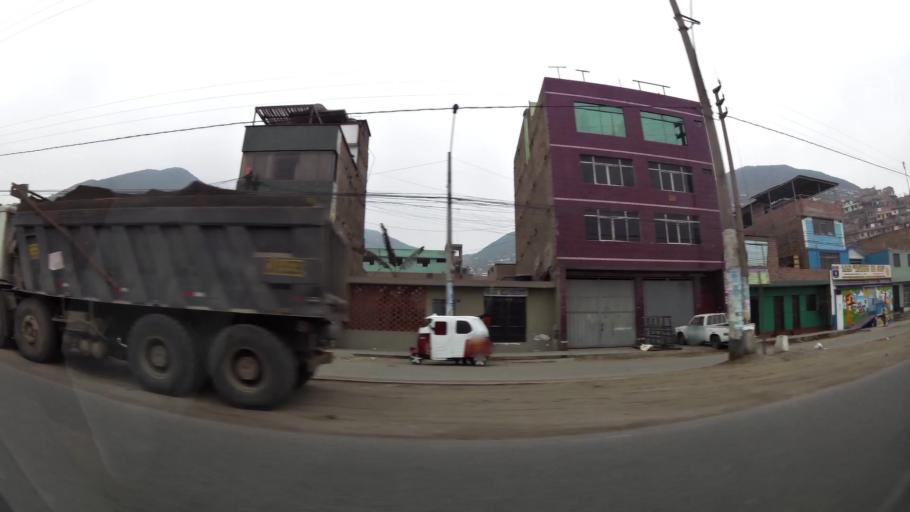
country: PE
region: Lima
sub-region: Lima
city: Urb. Santo Domingo
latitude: -11.9040
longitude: -77.0306
